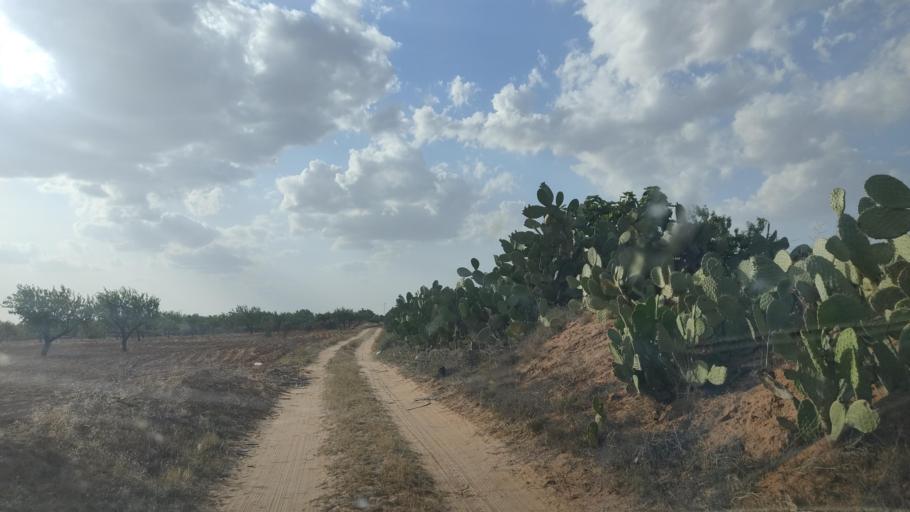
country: TN
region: Safaqis
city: Sfax
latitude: 34.8528
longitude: 10.5926
